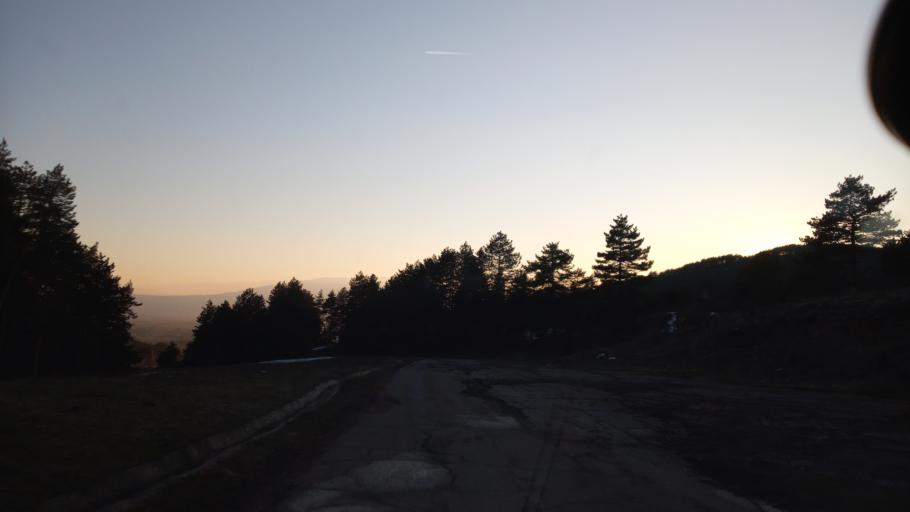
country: BG
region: Sofia-Capital
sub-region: Stolichna Obshtina
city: Bukhovo
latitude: 42.7927
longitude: 23.5249
